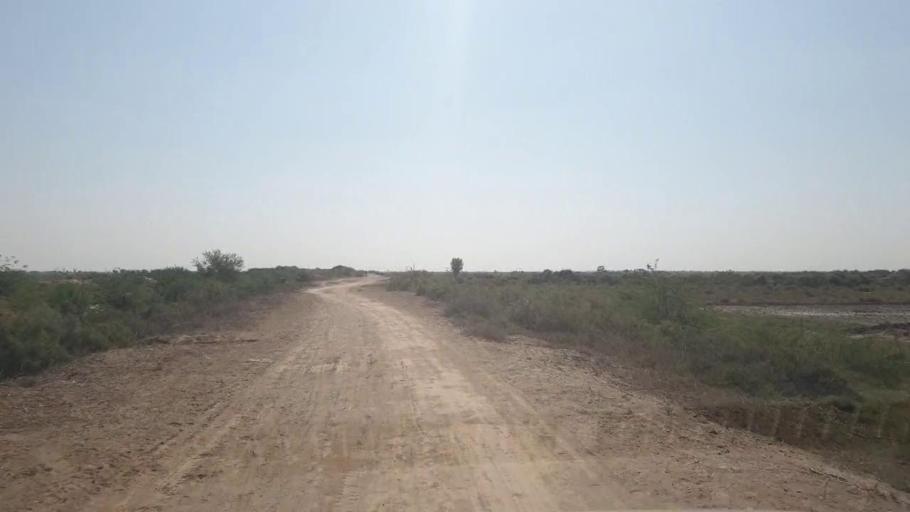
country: PK
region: Sindh
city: Tando Bago
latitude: 24.8782
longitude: 69.1644
